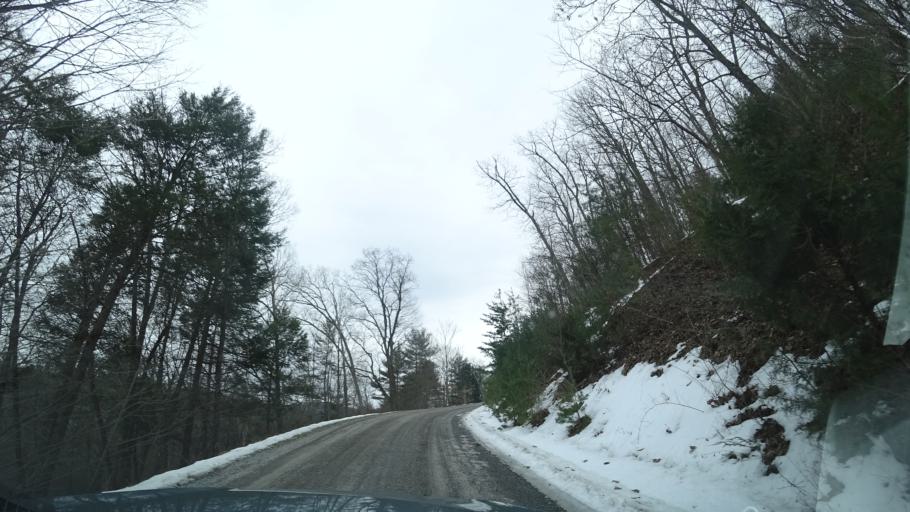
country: US
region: West Virginia
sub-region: Hardy County
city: Moorefield
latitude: 39.0213
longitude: -78.7718
